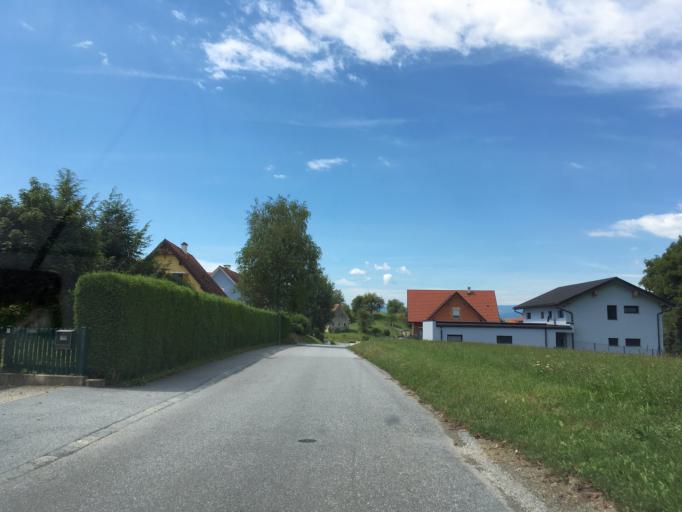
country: AT
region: Styria
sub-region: Politischer Bezirk Leibnitz
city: Pistorf
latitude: 46.7907
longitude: 15.3833
